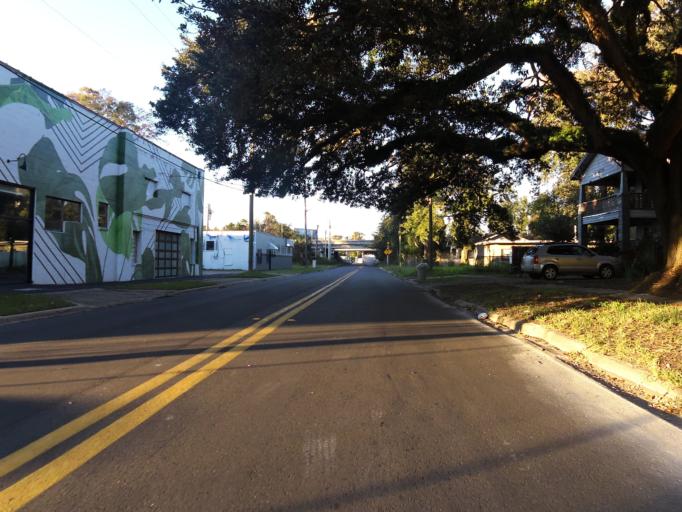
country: US
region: Florida
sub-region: Duval County
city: Jacksonville
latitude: 30.3204
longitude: -81.6970
